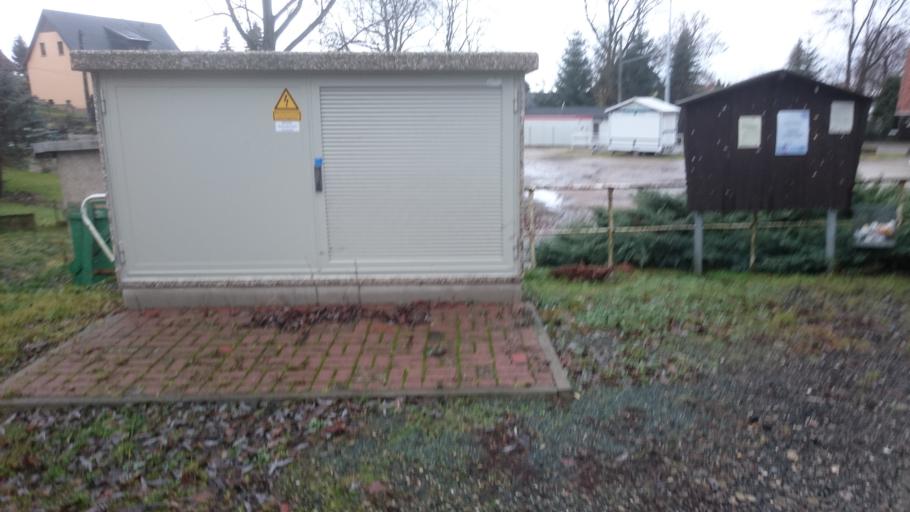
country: DE
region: Saxony
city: Mulsen
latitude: 50.7511
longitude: 12.5274
